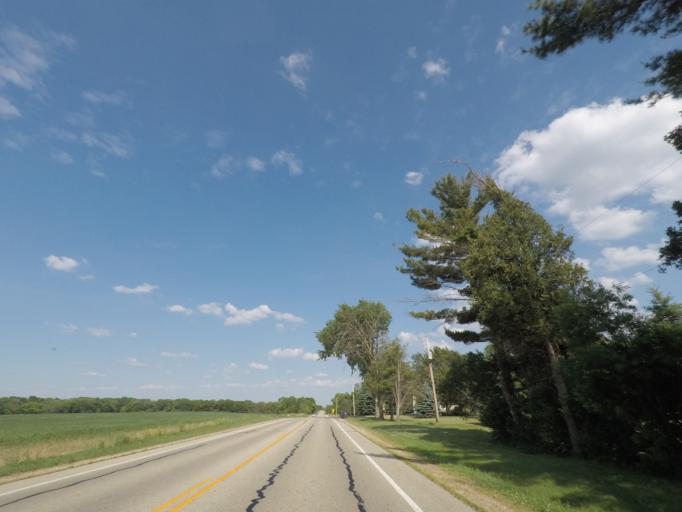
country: US
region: Wisconsin
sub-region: Waukesha County
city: Eagle
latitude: 42.7933
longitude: -88.5133
